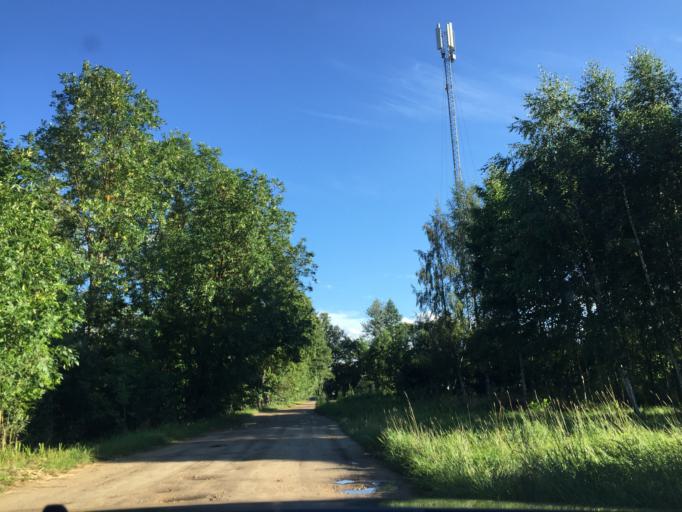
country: LV
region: Riga
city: Jaunciems
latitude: 57.0538
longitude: 24.1316
